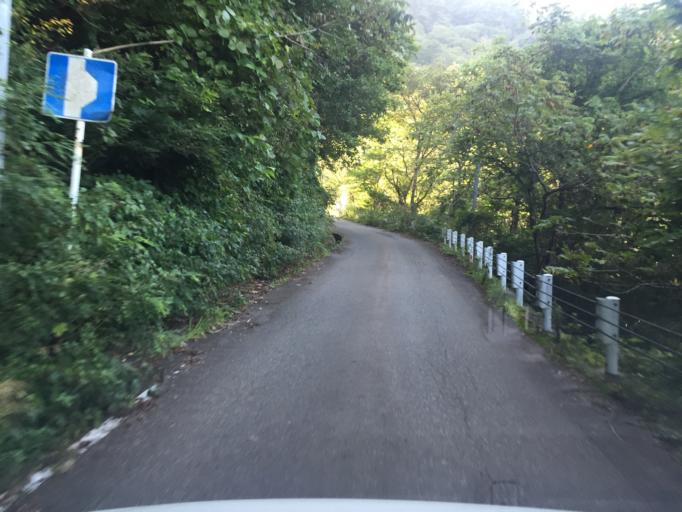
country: JP
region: Fukushima
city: Inawashiro
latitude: 37.4287
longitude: 139.9828
